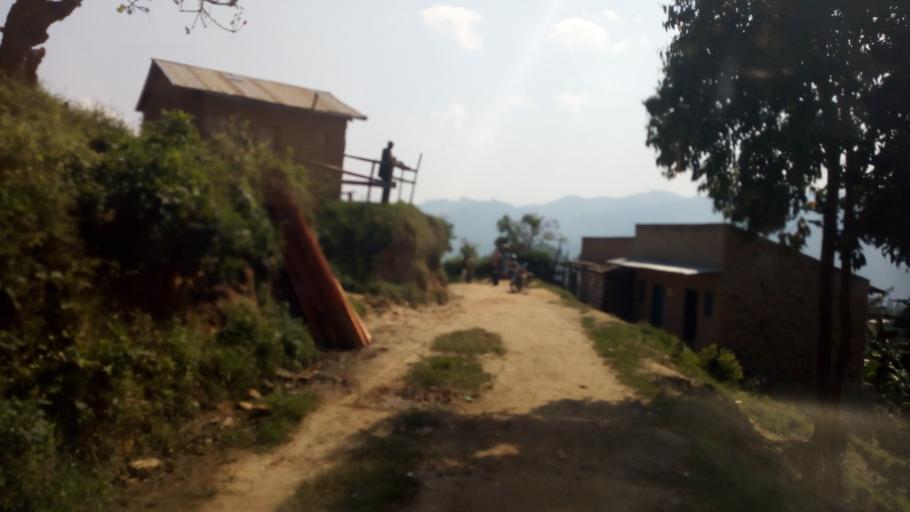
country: UG
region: Western Region
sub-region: Kisoro District
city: Kisoro
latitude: -1.1109
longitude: 29.5926
